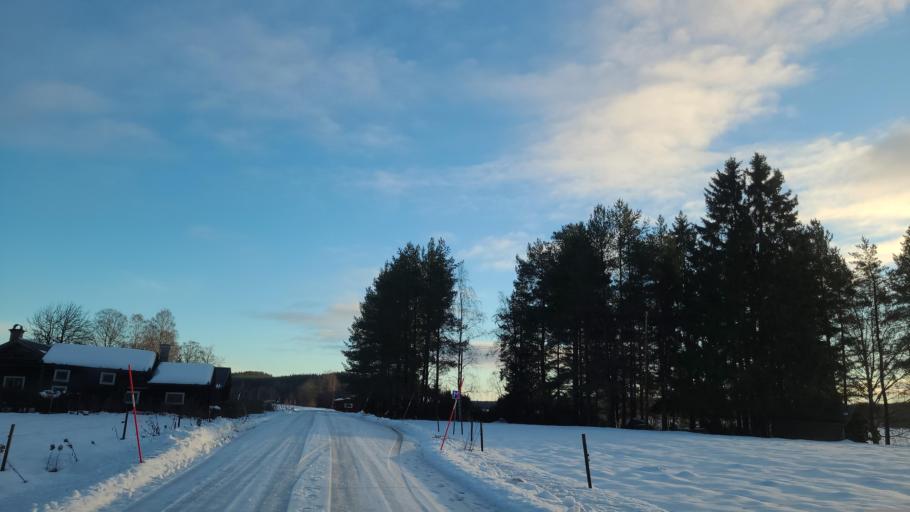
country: SE
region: Gaevleborg
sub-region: Bollnas Kommun
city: Kilafors
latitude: 61.3975
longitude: 16.6690
